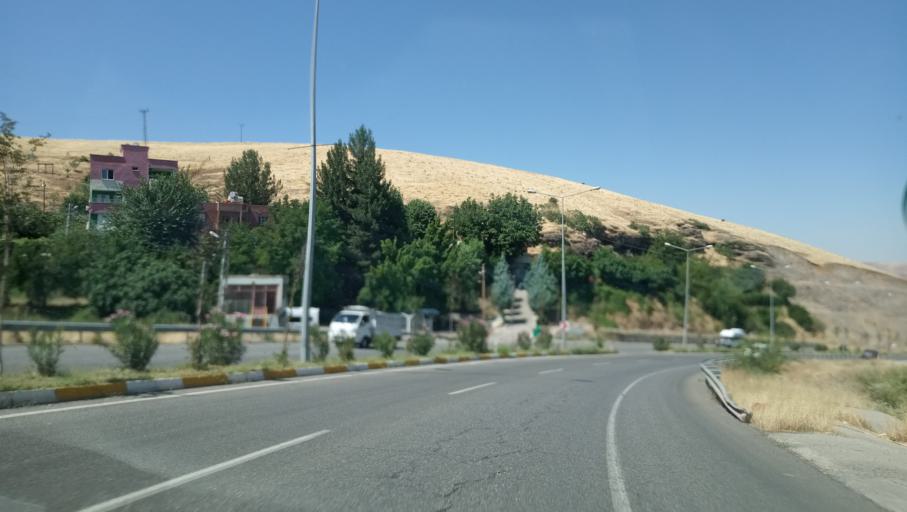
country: TR
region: Siirt
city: Civankan
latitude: 37.9479
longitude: 41.8756
